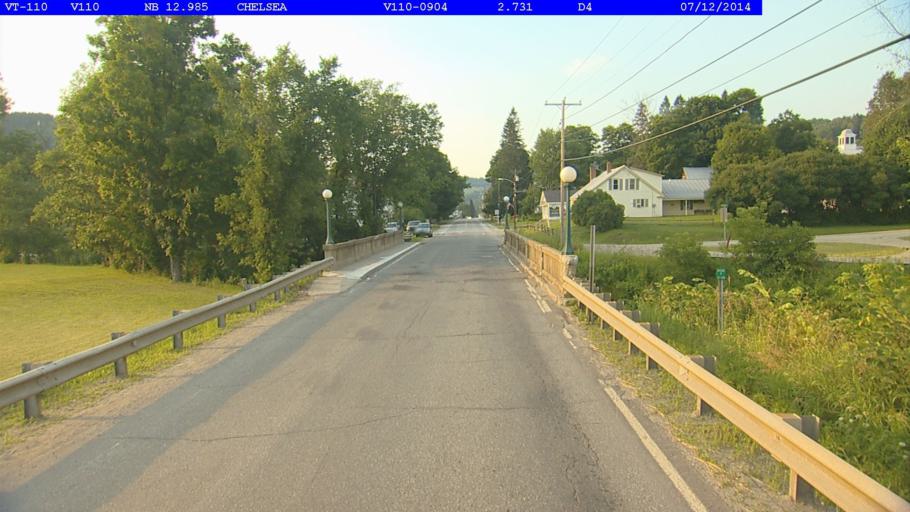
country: US
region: Vermont
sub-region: Orange County
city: Chelsea
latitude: 43.9857
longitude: -72.4482
